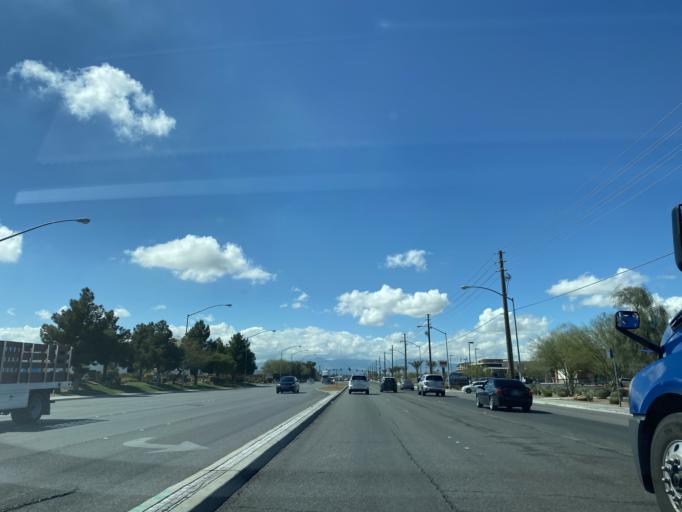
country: US
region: Nevada
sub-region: Clark County
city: North Las Vegas
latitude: 36.2398
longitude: -115.1213
